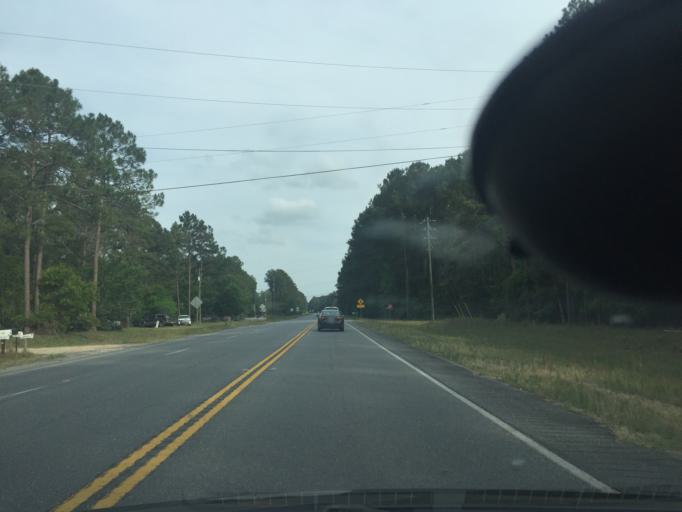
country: US
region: Georgia
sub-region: Chatham County
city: Bloomingdale
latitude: 32.0500
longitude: -81.3402
